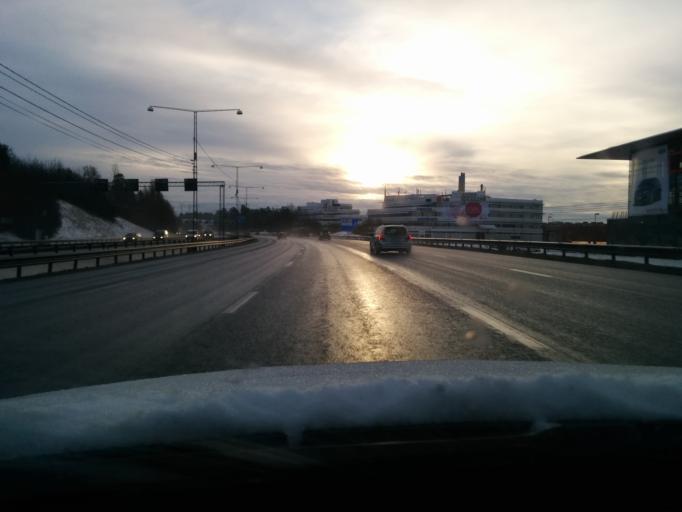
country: SE
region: Stockholm
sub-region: Sollentuna Kommun
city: Sollentuna
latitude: 59.4222
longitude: 17.9249
